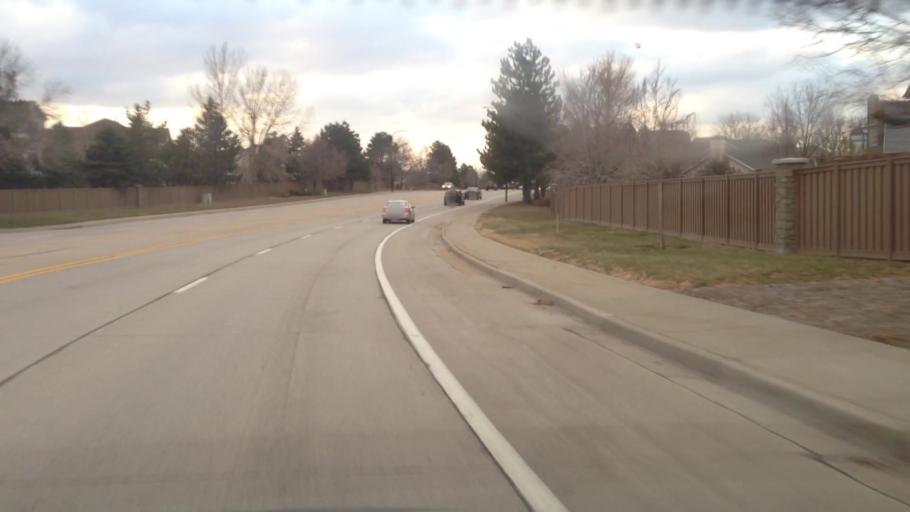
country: US
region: Colorado
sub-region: Douglas County
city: Carriage Club
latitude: 39.5369
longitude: -104.9067
